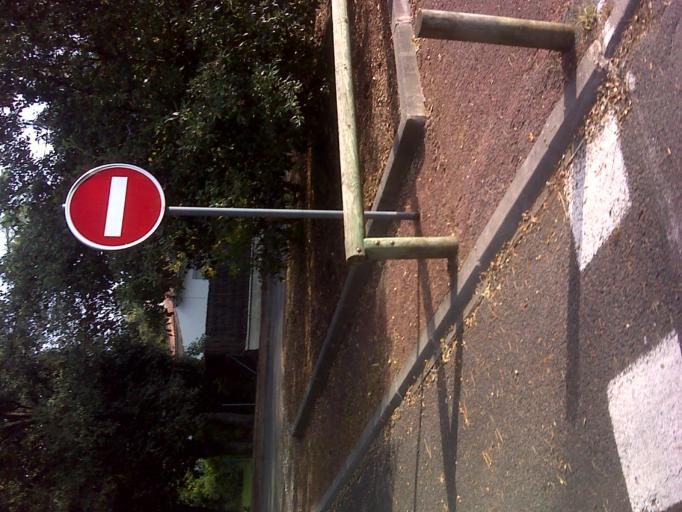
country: FR
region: Poitou-Charentes
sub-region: Departement de la Charente-Maritime
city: Saint-Palais-sur-Mer
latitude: 45.6453
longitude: -1.0961
